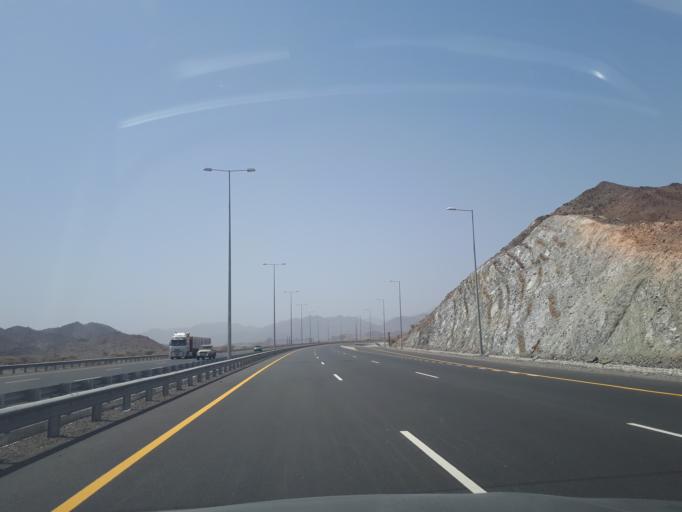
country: OM
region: Muhafazat ad Dakhiliyah
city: Bidbid
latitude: 23.3205
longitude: 58.1153
